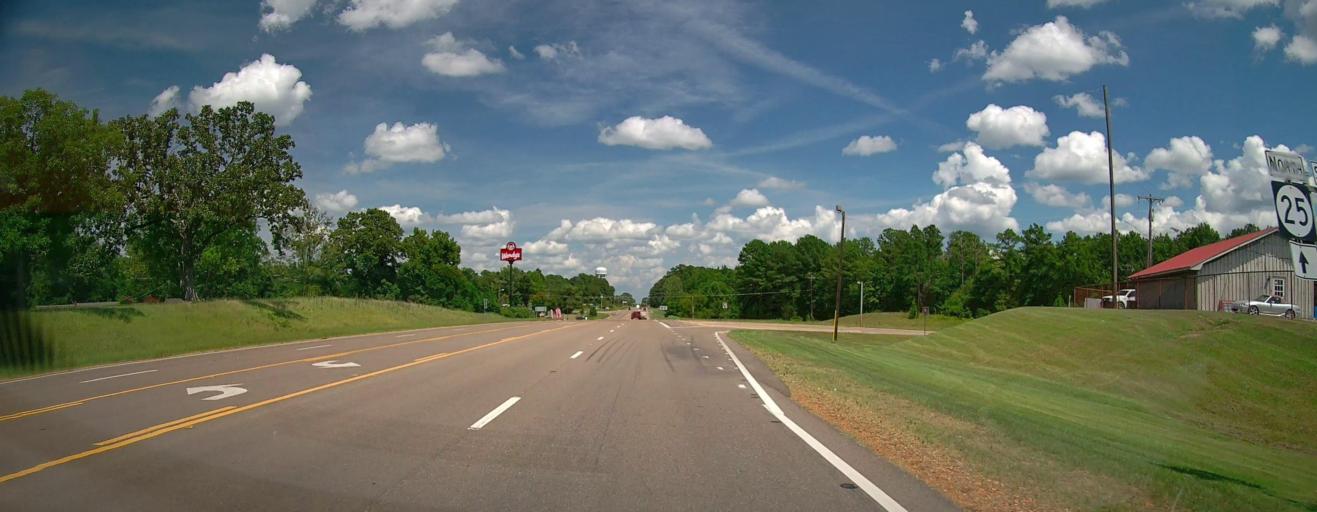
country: US
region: Mississippi
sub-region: Monroe County
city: Aberdeen
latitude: 33.8148
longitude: -88.5667
